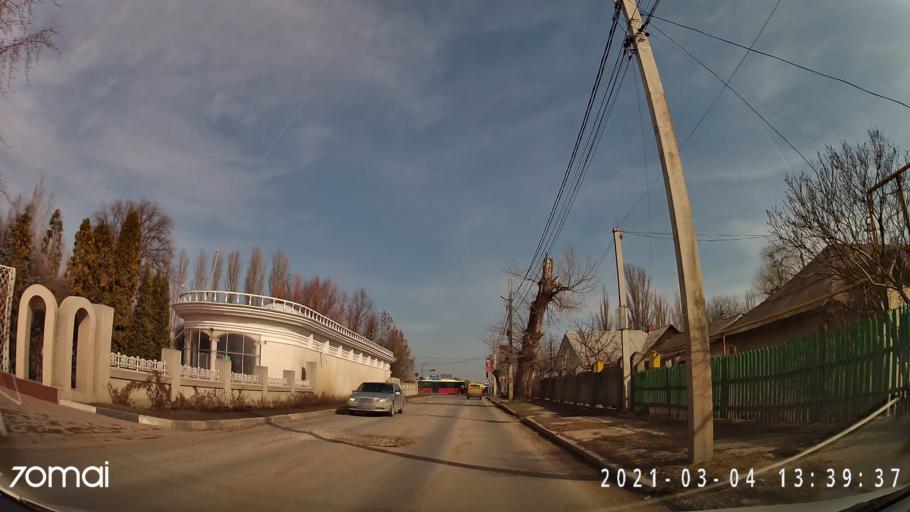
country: MD
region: Balti
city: Balti
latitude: 47.7783
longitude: 27.9478
